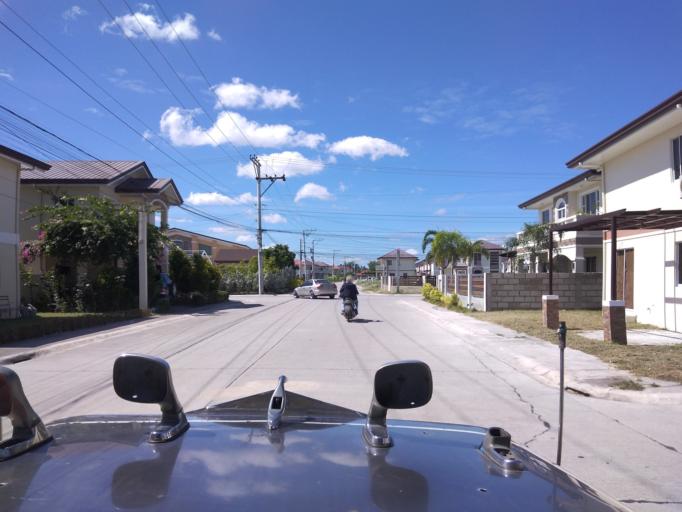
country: PH
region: Central Luzon
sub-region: Province of Pampanga
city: San Juan
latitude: 15.0202
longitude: 120.6631
